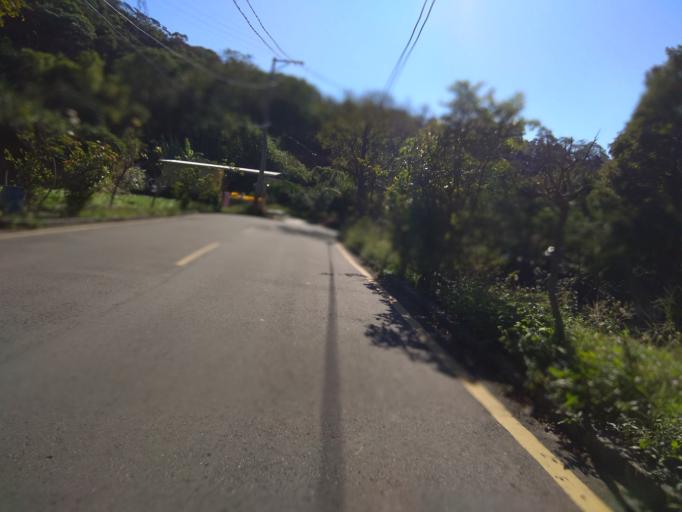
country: TW
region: Taiwan
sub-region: Hsinchu
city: Zhubei
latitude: 24.8593
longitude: 121.1050
